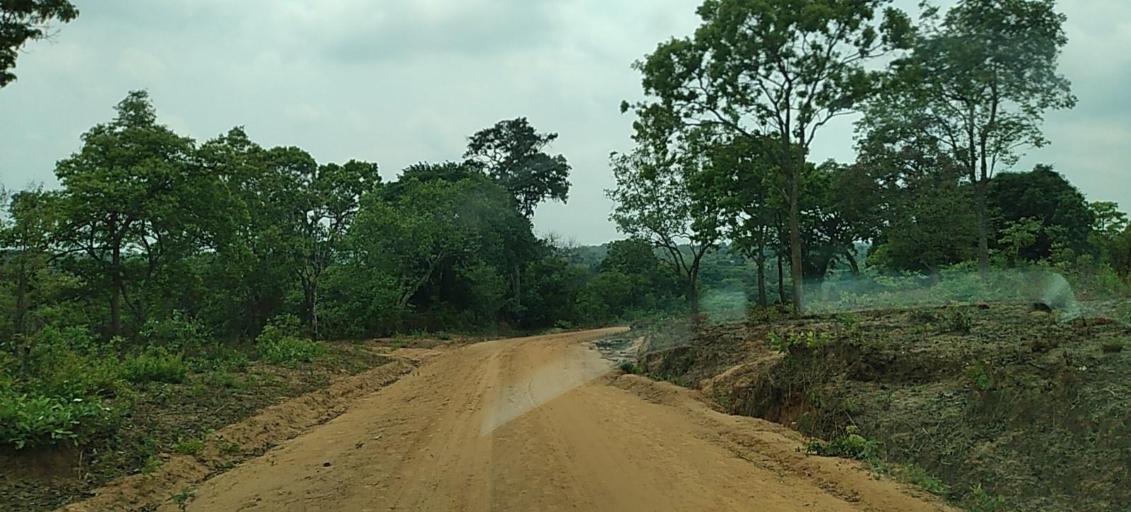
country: ZM
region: North-Western
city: Mwinilunga
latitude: -11.4613
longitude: 24.7606
